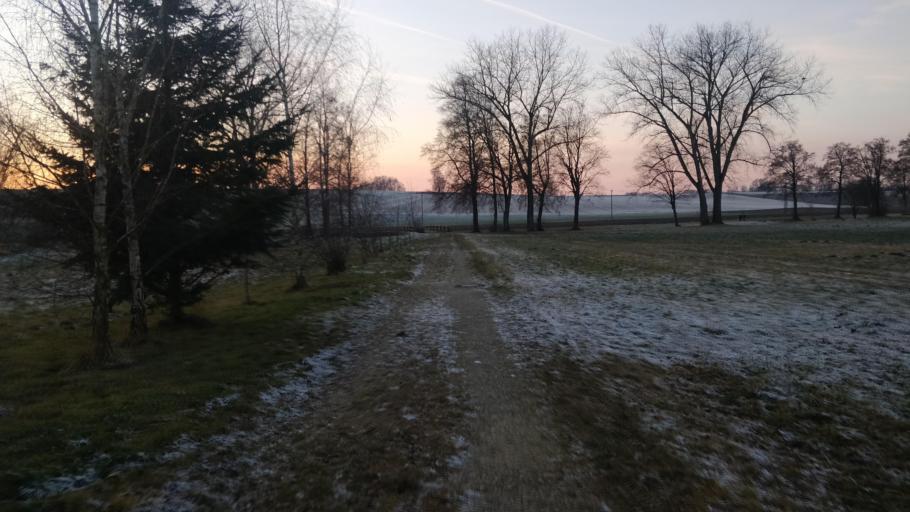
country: DE
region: Bavaria
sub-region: Upper Bavaria
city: Obertaufkirchen
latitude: 48.2618
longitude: 12.2723
